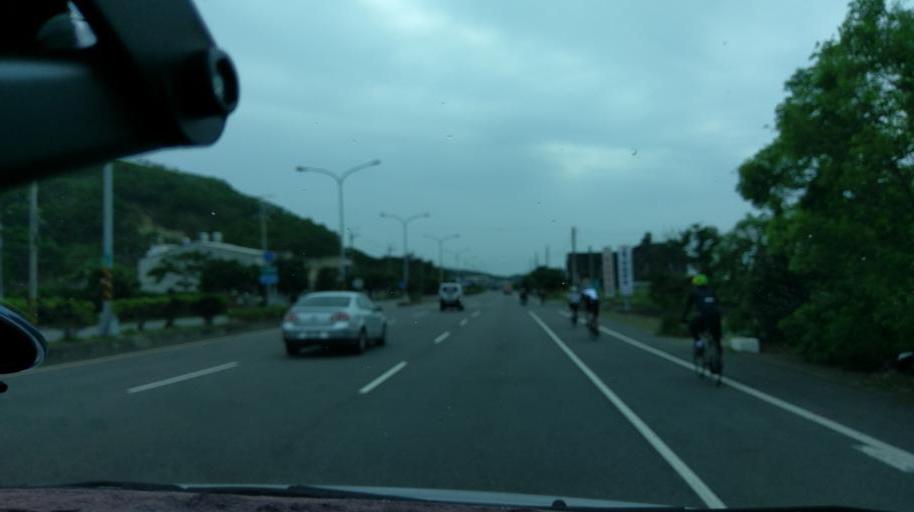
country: TW
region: Taiwan
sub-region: Miaoli
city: Miaoli
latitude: 24.5214
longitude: 120.6920
